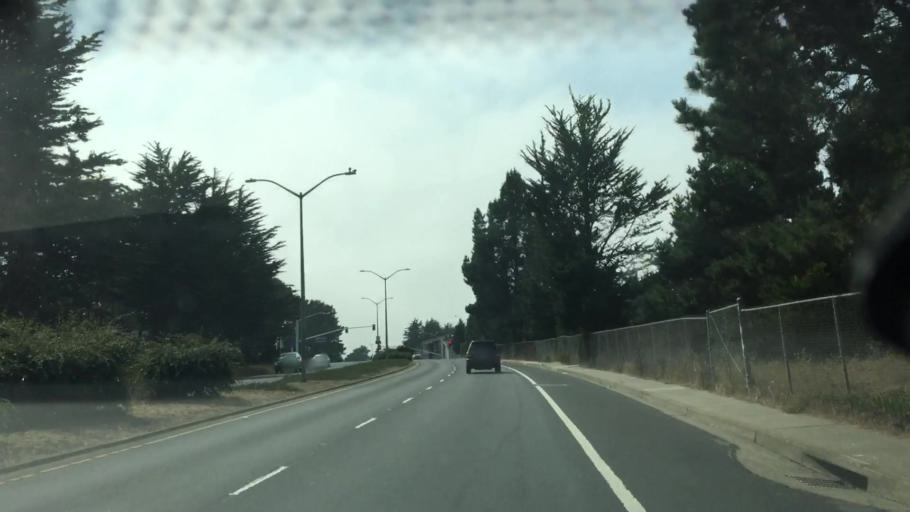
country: US
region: California
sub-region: San Mateo County
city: Colma
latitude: 37.6695
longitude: -122.4731
